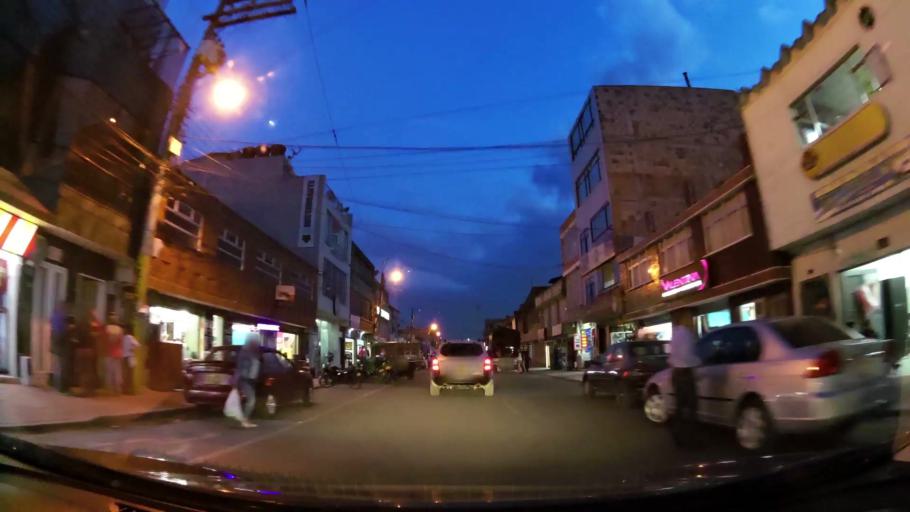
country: CO
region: Cundinamarca
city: Funza
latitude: 4.7145
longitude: -74.2109
